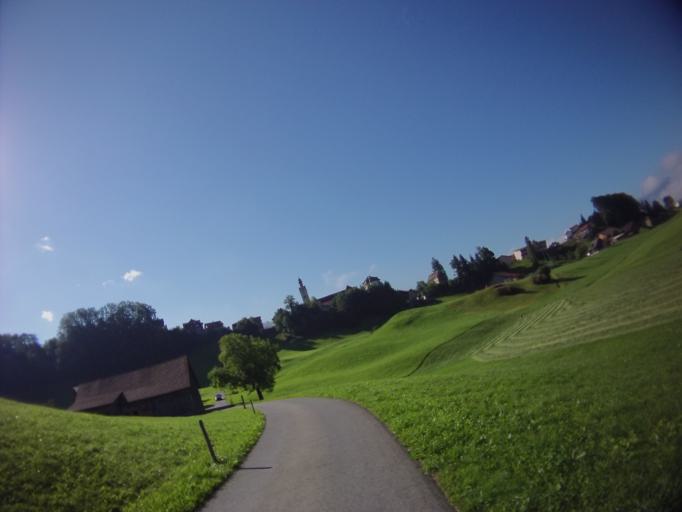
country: CH
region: Schwyz
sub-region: Bezirk Schwyz
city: Sattel
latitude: 47.0869
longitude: 8.6362
